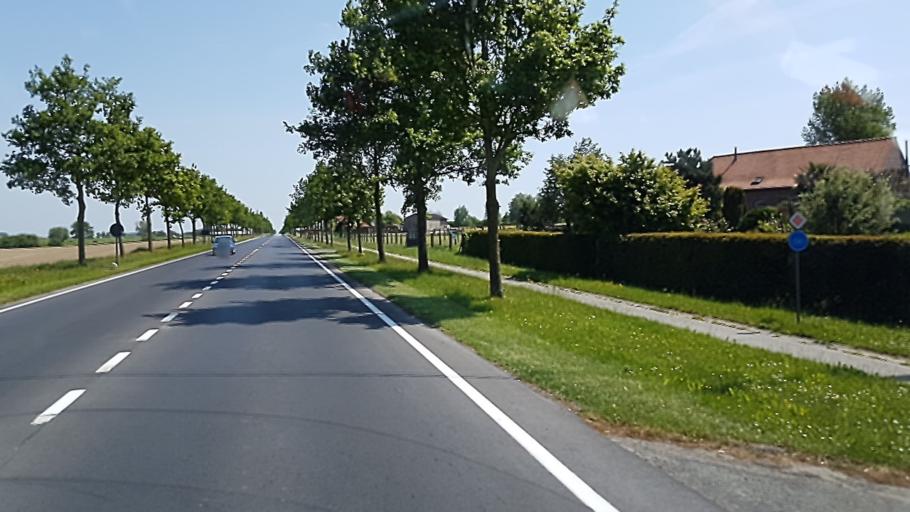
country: BE
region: Flanders
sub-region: Provincie West-Vlaanderen
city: Wervik
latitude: 50.8265
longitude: 3.0187
